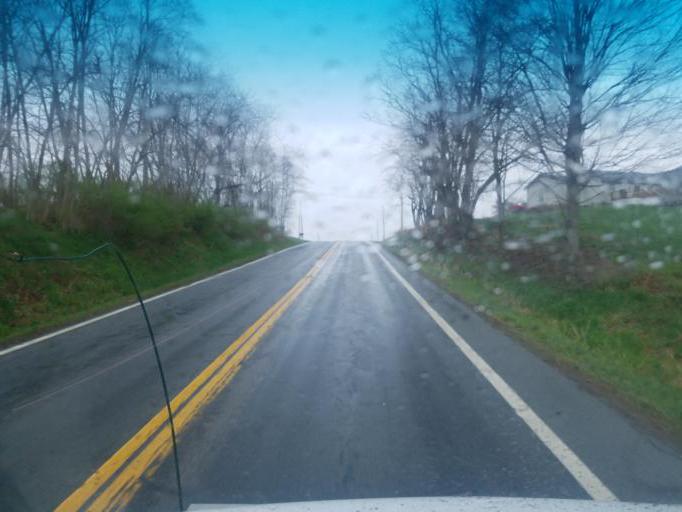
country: US
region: Ohio
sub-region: Wayne County
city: Wooster
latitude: 40.7544
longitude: -81.9302
